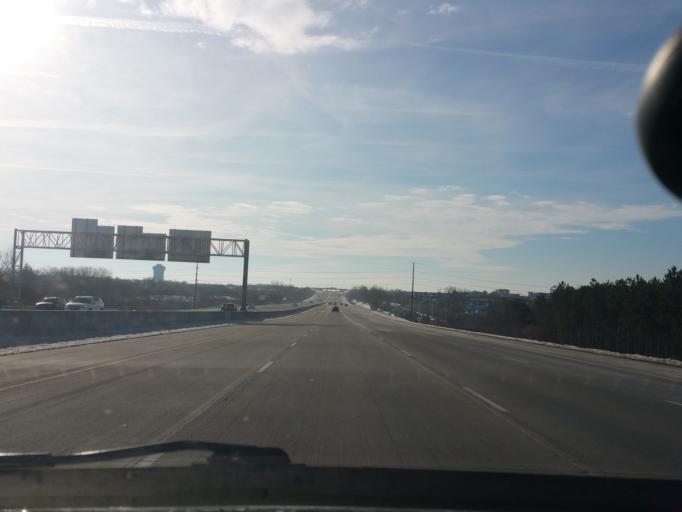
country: US
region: Iowa
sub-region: Polk County
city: Clive
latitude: 41.5780
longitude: -93.7774
